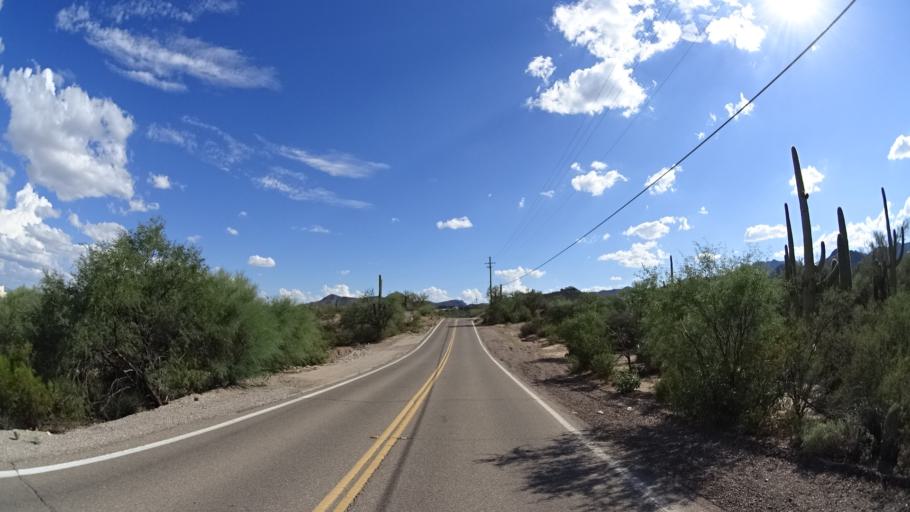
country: US
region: Arizona
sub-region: Pima County
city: Flowing Wells
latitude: 32.2632
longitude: -111.0628
